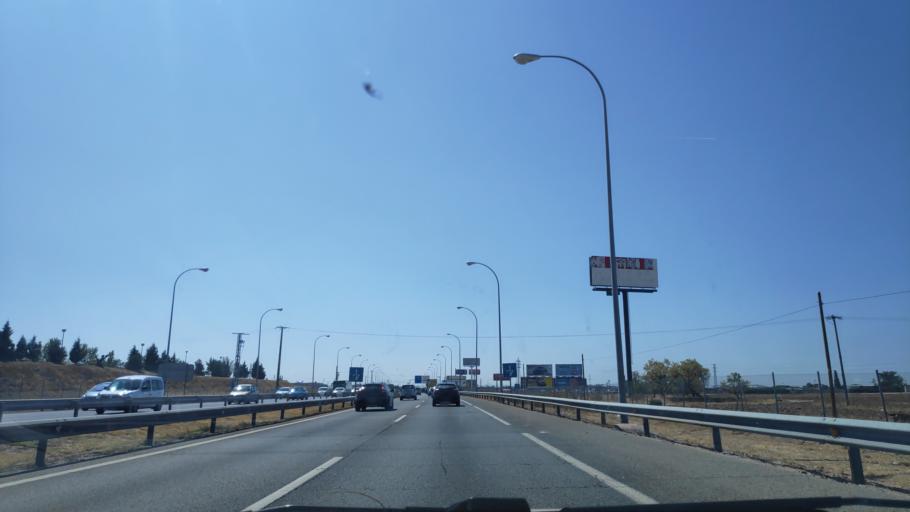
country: ES
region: Madrid
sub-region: Provincia de Madrid
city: Parla
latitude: 40.2329
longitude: -3.7829
